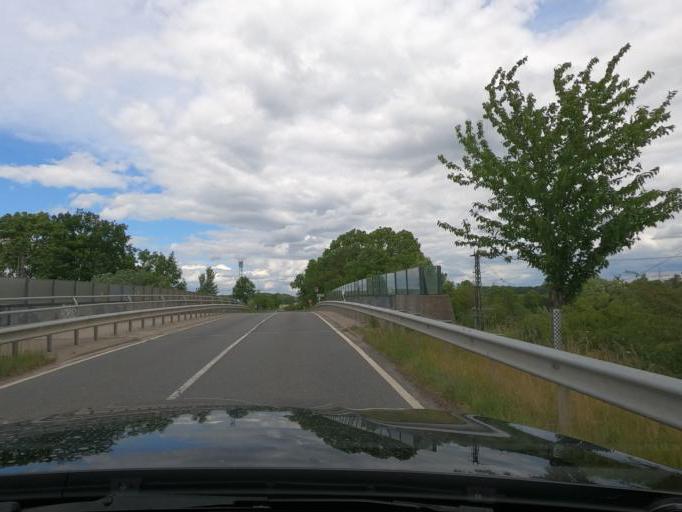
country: DE
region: Lower Saxony
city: Lehrte
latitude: 52.3771
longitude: 9.9242
